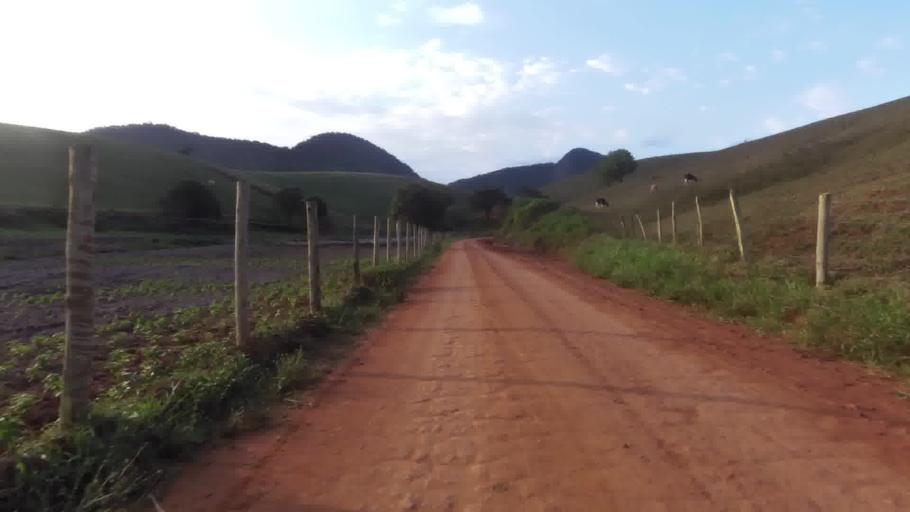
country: BR
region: Espirito Santo
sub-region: Alfredo Chaves
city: Alfredo Chaves
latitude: -20.6966
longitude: -40.6329
